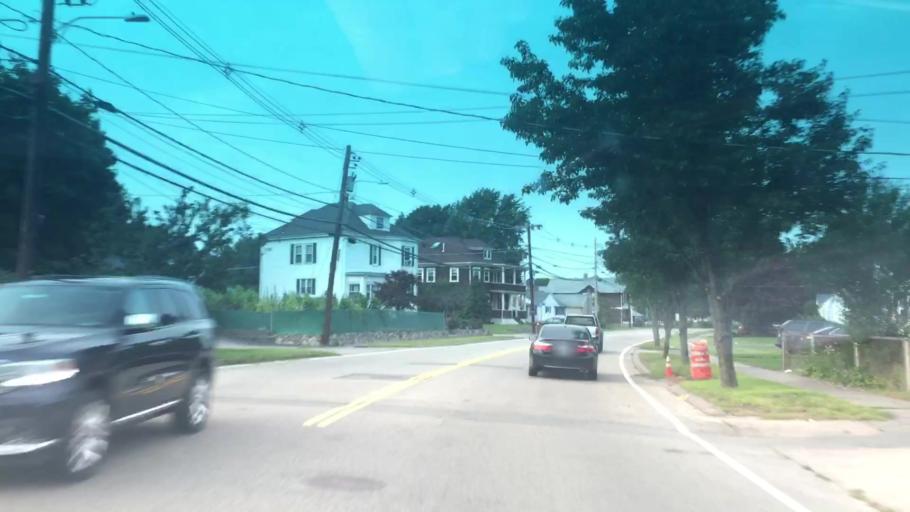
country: US
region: Massachusetts
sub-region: Norfolk County
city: Norwood
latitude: 42.1816
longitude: -71.1975
